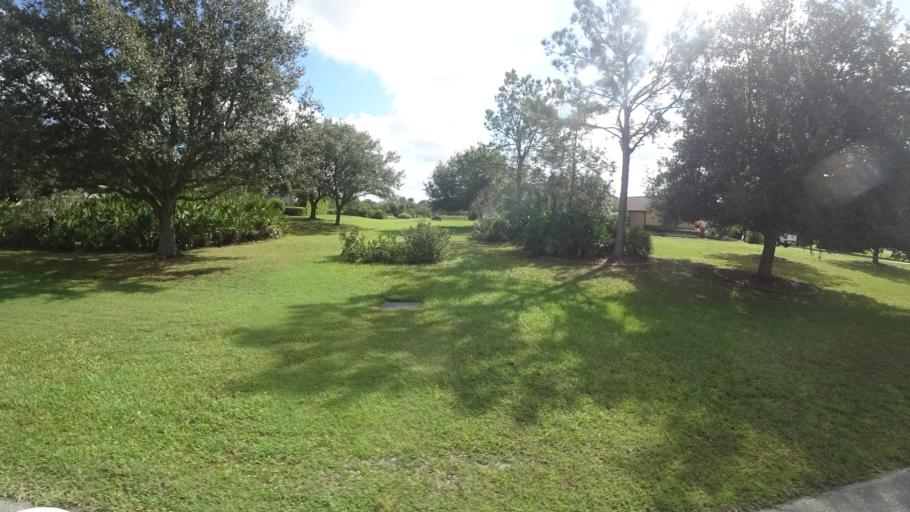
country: US
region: Florida
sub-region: Sarasota County
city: Fruitville
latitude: 27.3943
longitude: -82.3062
